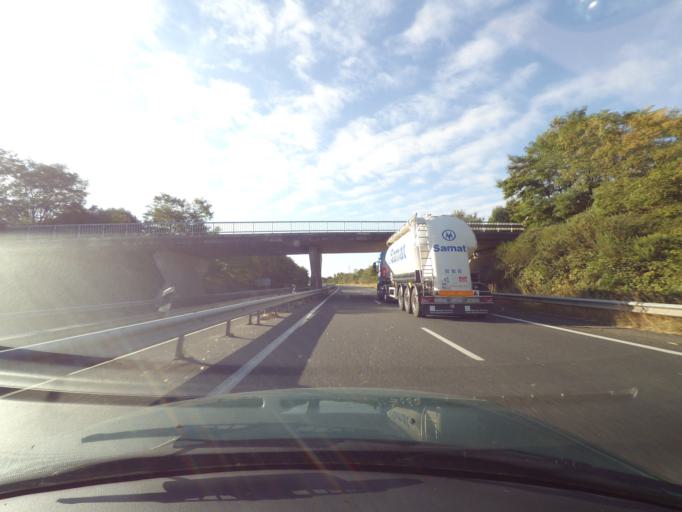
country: FR
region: Poitou-Charentes
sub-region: Departement des Deux-Sevres
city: Bressuire
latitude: 46.8431
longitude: -0.4673
